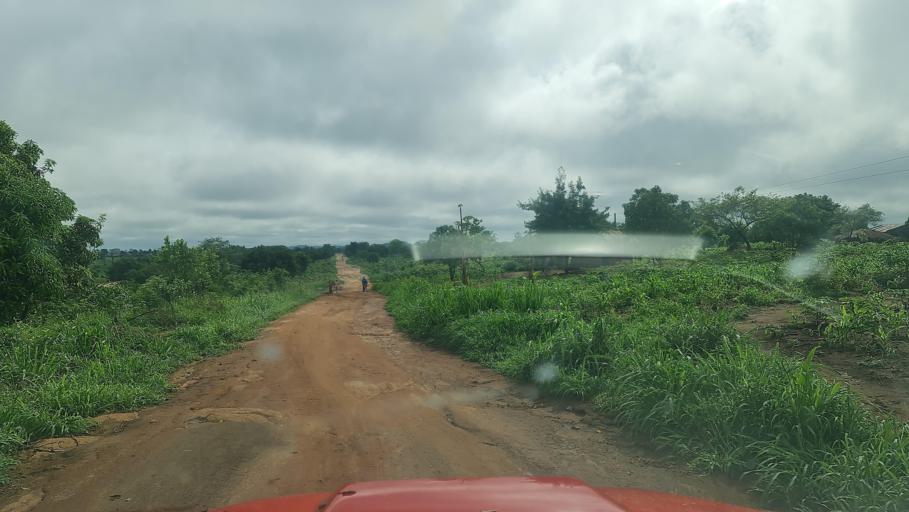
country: MW
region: Southern Region
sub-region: Nsanje District
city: Nsanje
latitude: -17.2224
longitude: 35.6661
